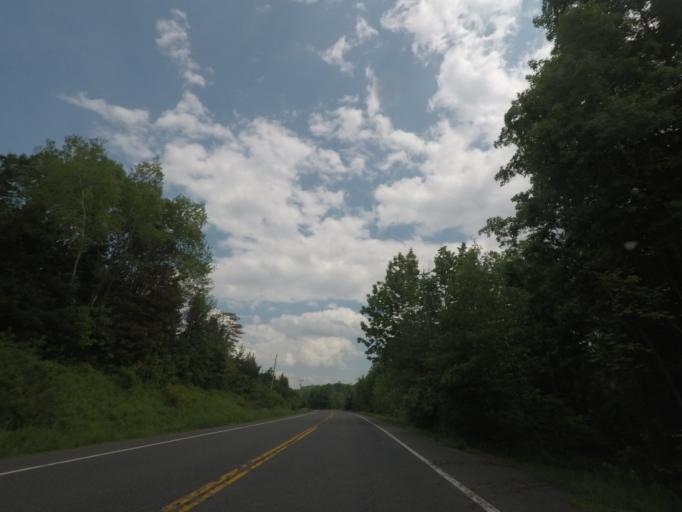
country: US
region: New York
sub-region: Columbia County
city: Philmont
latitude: 42.1150
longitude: -73.7107
